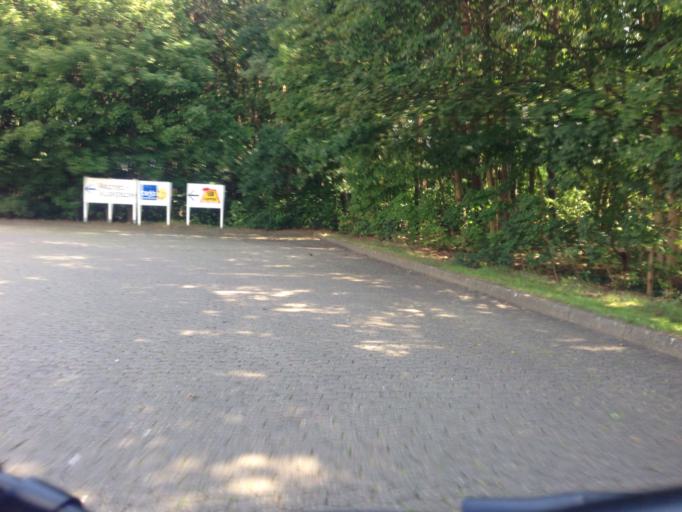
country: DE
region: Lower Saxony
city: Adendorf
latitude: 53.2868
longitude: 10.4299
